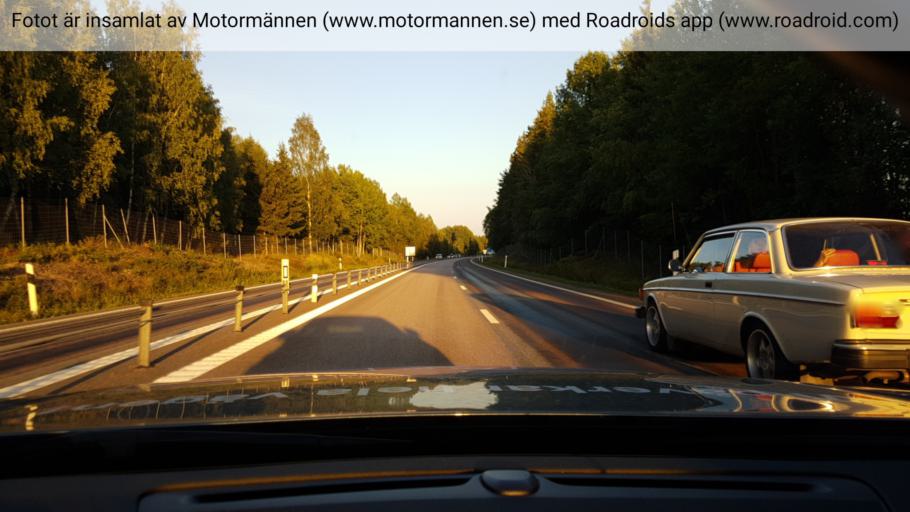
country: SE
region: Vaestmanland
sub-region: Vasteras
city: Skultuna
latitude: 59.6618
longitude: 16.3573
